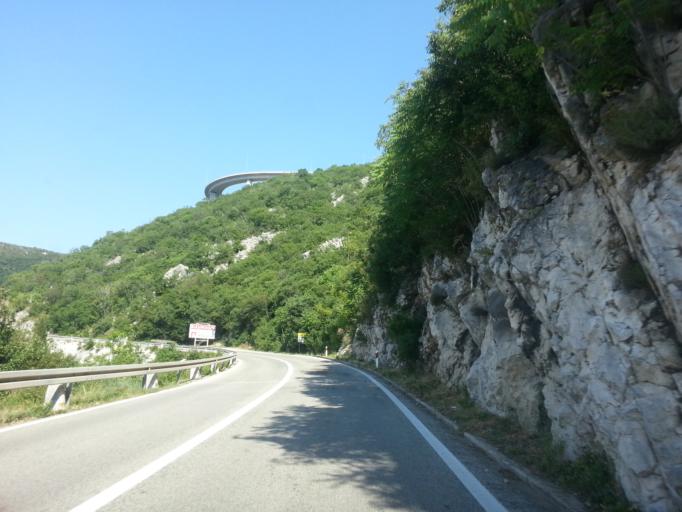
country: HR
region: Primorsko-Goranska
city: Bakar
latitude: 45.3094
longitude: 14.5371
